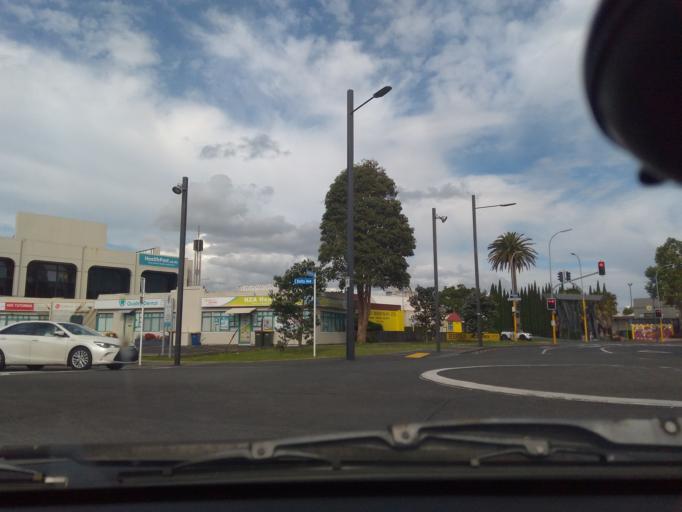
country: NZ
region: Auckland
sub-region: Auckland
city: Waitakere
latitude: -36.9072
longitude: 174.6827
